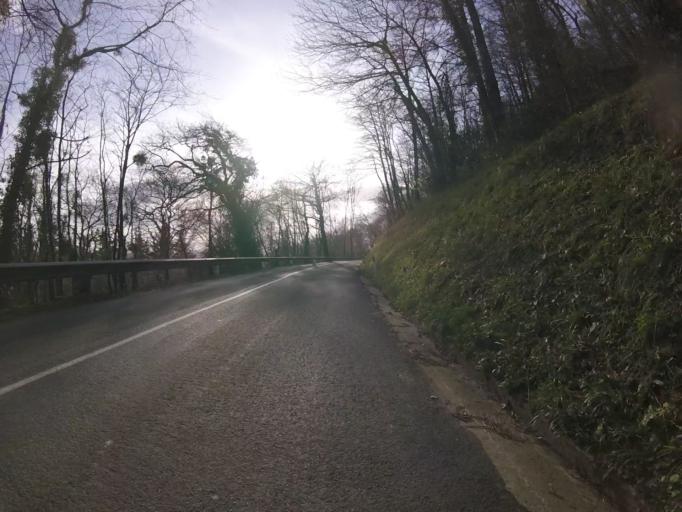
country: ES
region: Basque Country
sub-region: Provincia de Guipuzcoa
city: Asteasu
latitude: 43.2028
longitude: -2.1160
